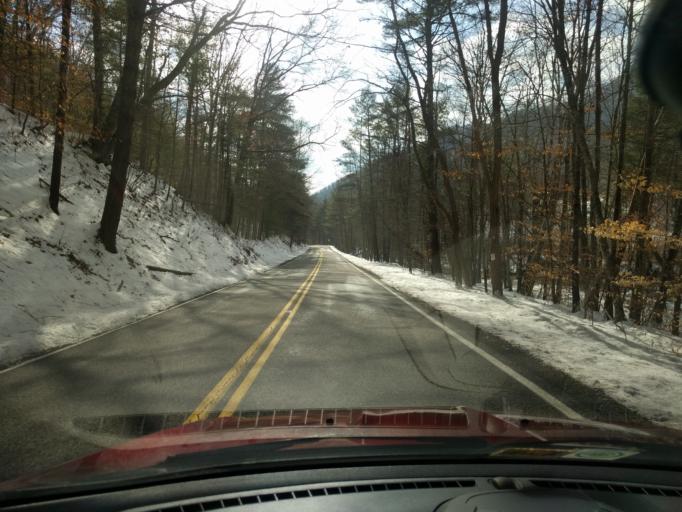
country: US
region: Virginia
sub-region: Bath County
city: Warm Springs
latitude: 38.1158
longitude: -79.9142
